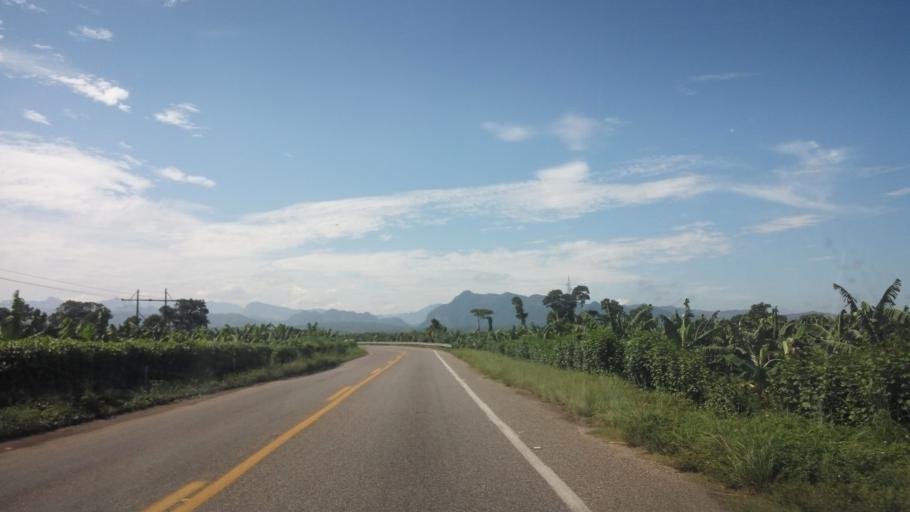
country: MX
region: Tabasco
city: Teapa
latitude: 17.6059
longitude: -92.9665
